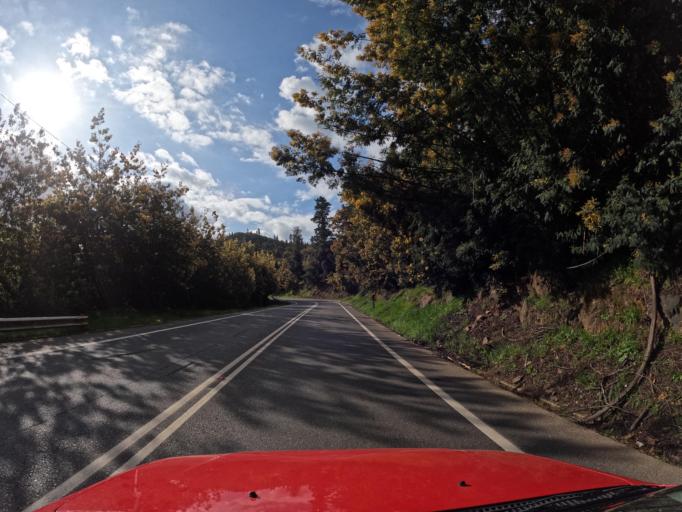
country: CL
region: Maule
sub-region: Provincia de Talca
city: Constitucion
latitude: -35.5400
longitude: -72.1559
